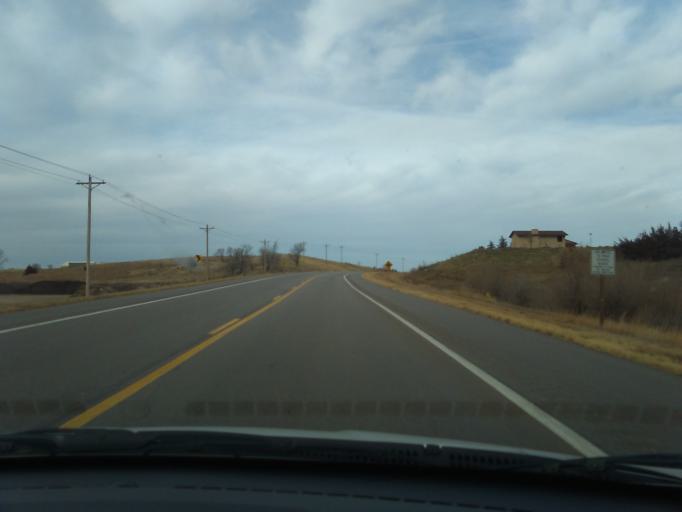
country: US
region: Nebraska
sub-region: Dundy County
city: Benkelman
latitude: 40.0495
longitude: -101.5437
